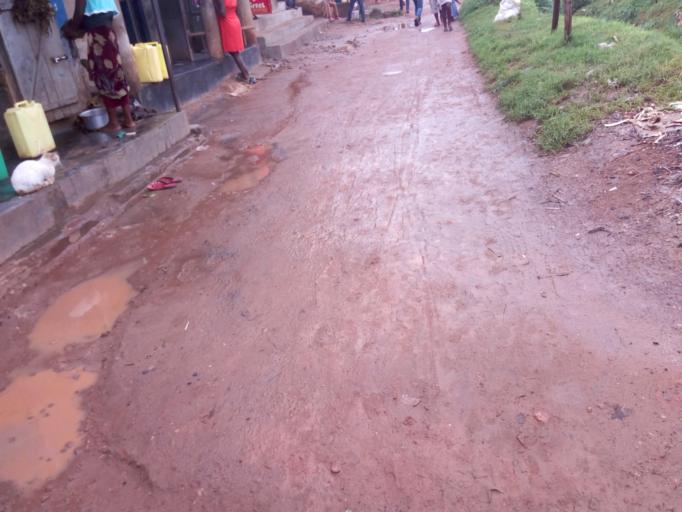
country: UG
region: Central Region
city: Kampala Central Division
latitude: 0.3349
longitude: 32.5595
